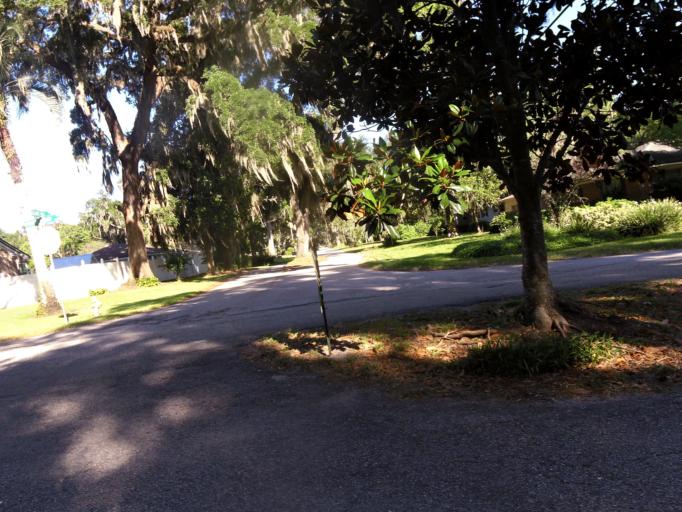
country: US
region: Florida
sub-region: Duval County
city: Jacksonville
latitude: 30.3154
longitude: -81.6163
